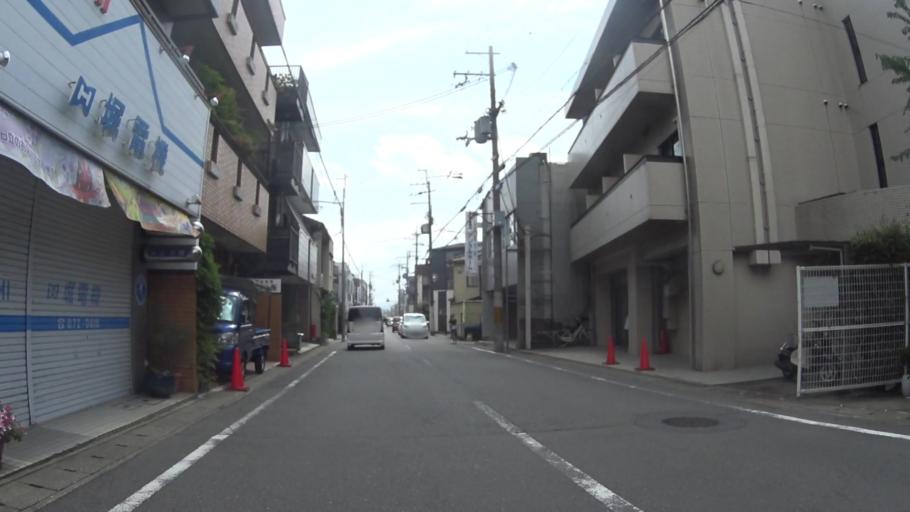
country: JP
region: Kyoto
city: Kyoto
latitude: 35.0131
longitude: 135.7120
